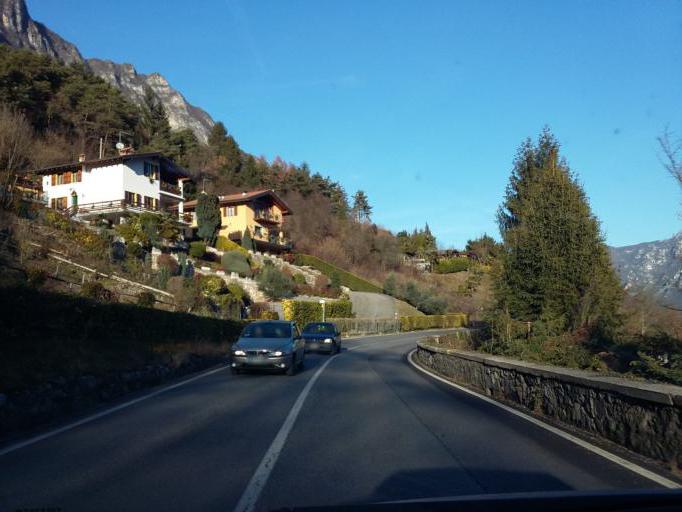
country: IT
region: Lombardy
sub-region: Provincia di Brescia
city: Crone
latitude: 45.7454
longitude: 10.4732
